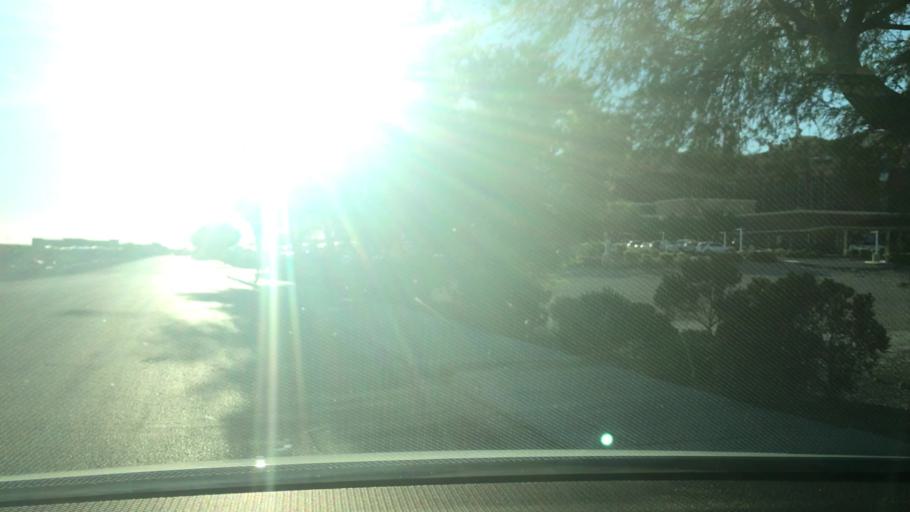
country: US
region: Nevada
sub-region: Clark County
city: Summerlin South
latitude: 36.0739
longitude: -115.2974
